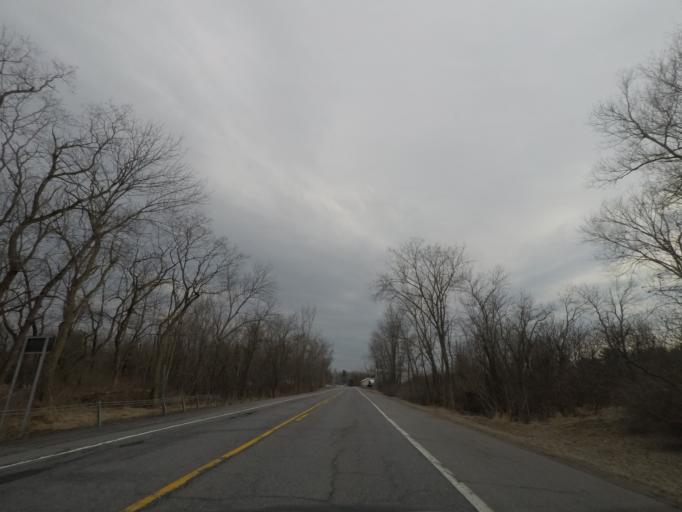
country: US
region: New York
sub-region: Saratoga County
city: Schuylerville
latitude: 43.1664
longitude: -73.5787
